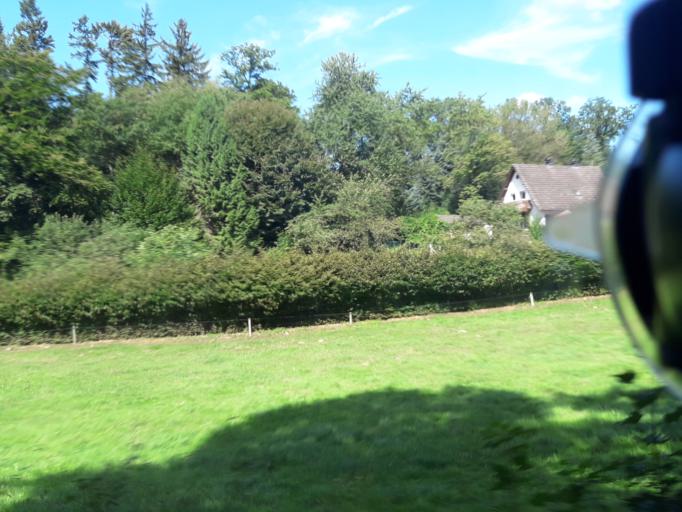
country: DE
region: North Rhine-Westphalia
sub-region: Regierungsbezirk Detmold
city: Paderborn
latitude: 51.6596
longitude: 8.7701
